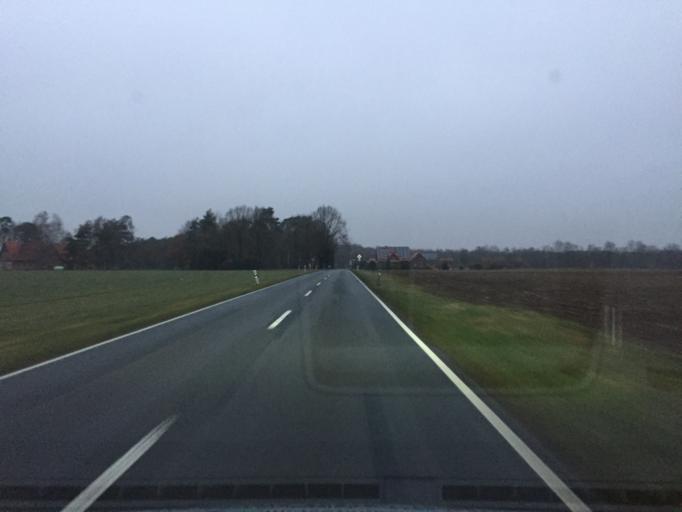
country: DE
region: Lower Saxony
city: Kirchdorf
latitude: 52.6156
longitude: 8.8935
